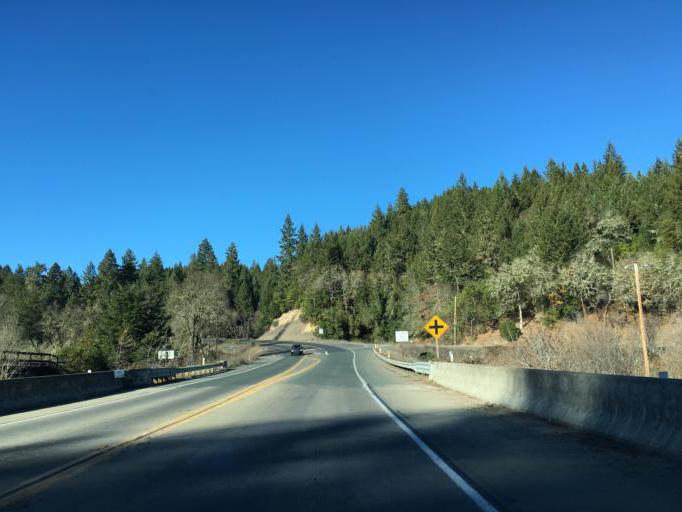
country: US
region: California
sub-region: Mendocino County
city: Brooktrails
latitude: 39.4632
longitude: -123.3504
